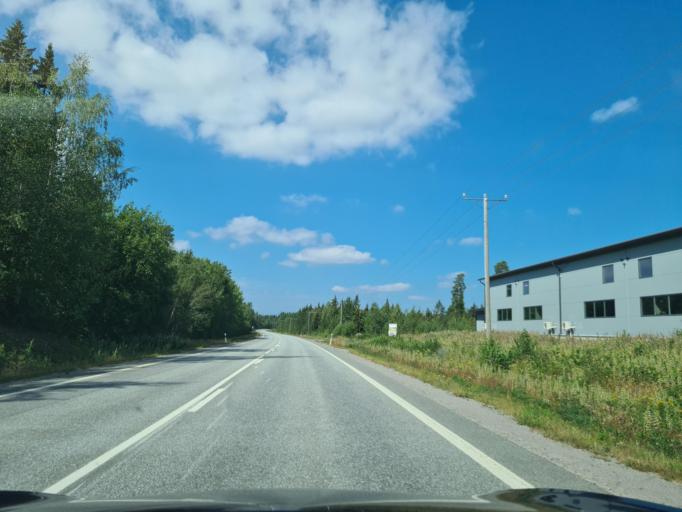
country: FI
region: Ostrobothnia
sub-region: Vaasa
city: Vaasa
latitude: 63.1681
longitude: 21.5872
